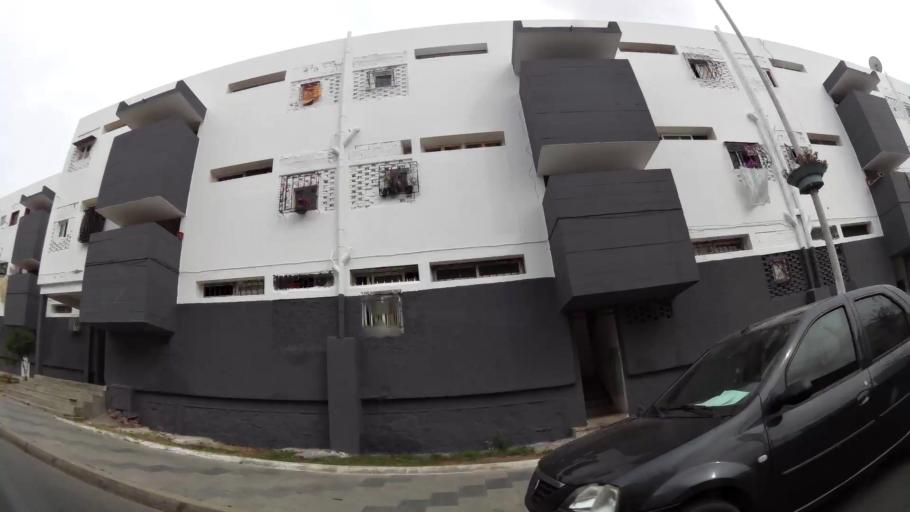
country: MA
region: Rabat-Sale-Zemmour-Zaer
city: Sale
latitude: 34.0477
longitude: -6.8007
